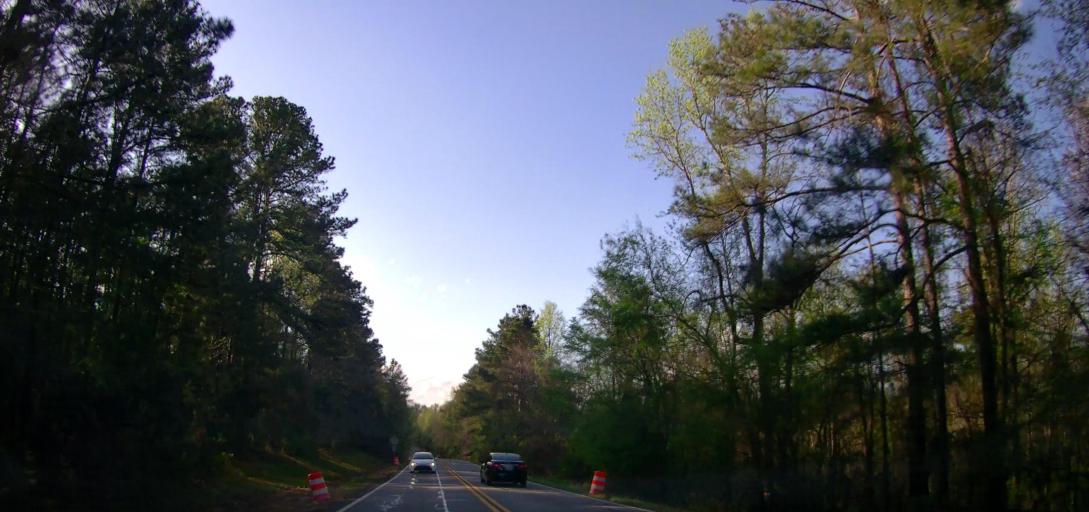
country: US
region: Georgia
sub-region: Baldwin County
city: Milledgeville
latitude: 33.1200
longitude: -83.2909
